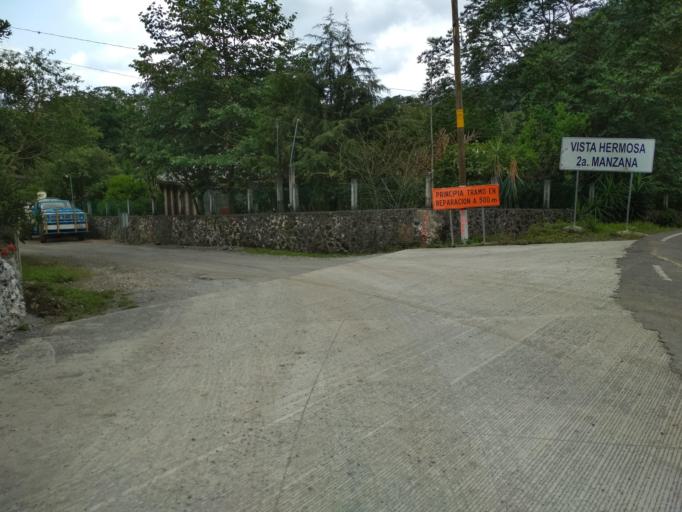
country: MX
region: Veracruz
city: Jilotepec
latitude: 19.6174
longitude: -96.9334
